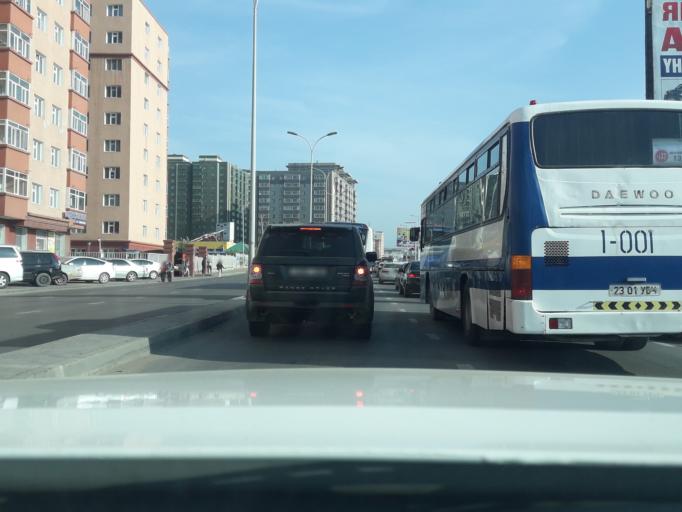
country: MN
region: Ulaanbaatar
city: Ulaanbaatar
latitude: 47.9061
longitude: 106.9434
